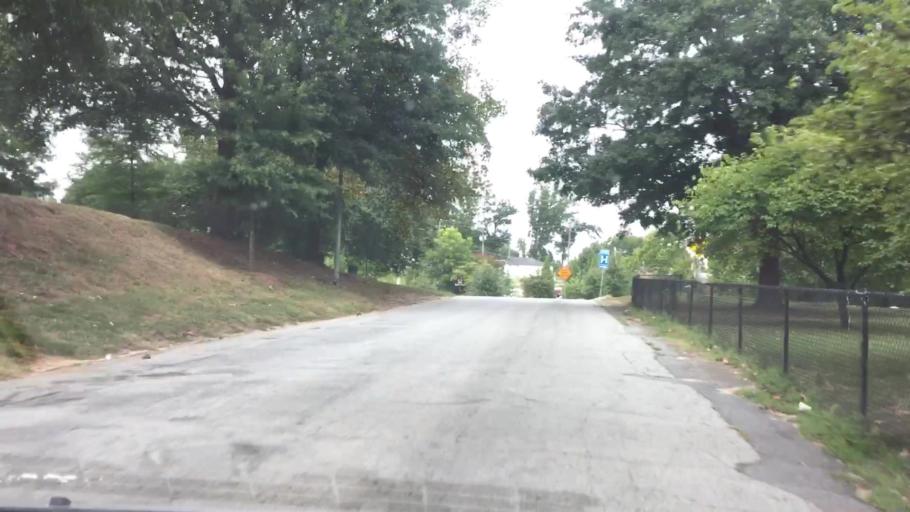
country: US
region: Georgia
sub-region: Fulton County
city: Atlanta
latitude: 33.7715
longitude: -84.4254
